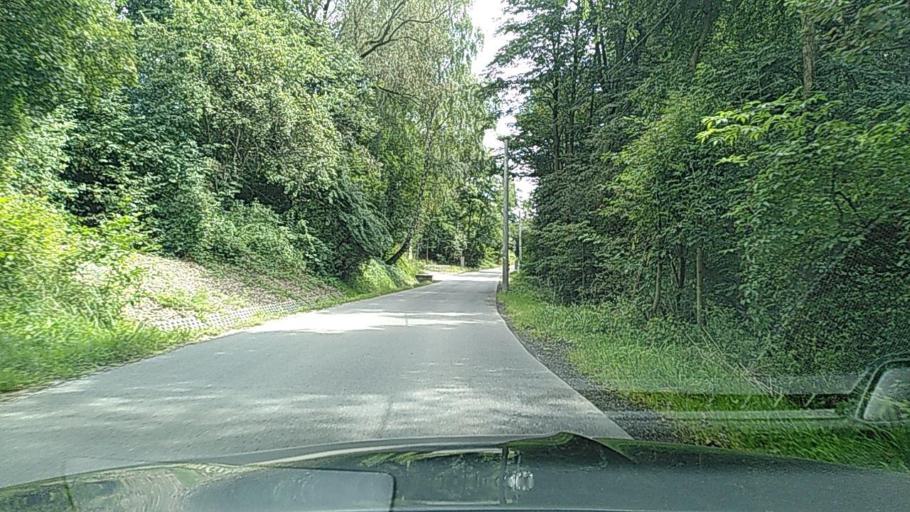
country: PL
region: Lesser Poland Voivodeship
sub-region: Powiat krakowski
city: Rzaska
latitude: 50.0906
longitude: 19.8704
